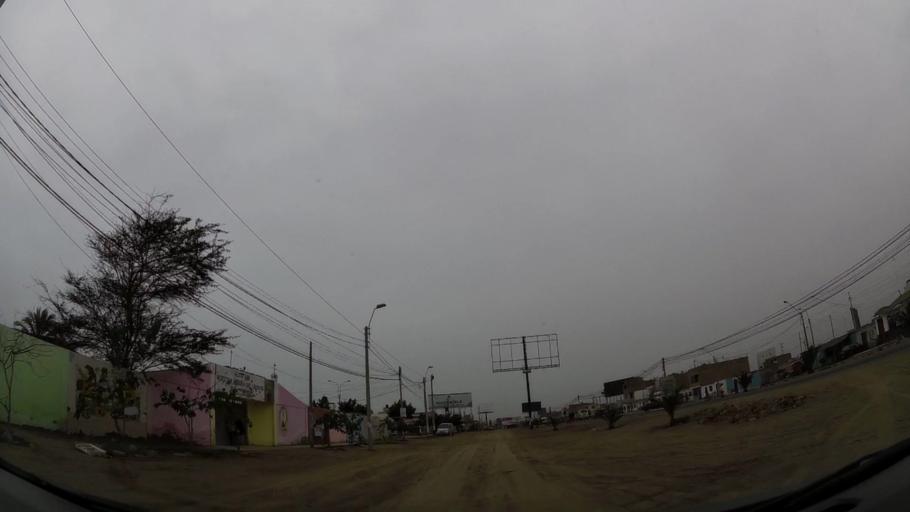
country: PE
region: Lima
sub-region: Lima
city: Punta Hermosa
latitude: -12.3147
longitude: -76.8336
